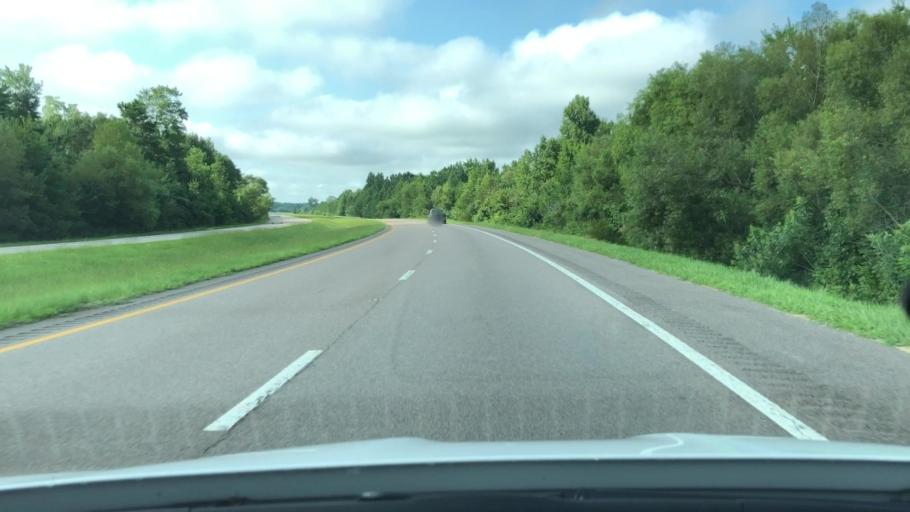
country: US
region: Virginia
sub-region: City of Portsmouth
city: Portsmouth Heights
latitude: 36.6682
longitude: -76.3549
